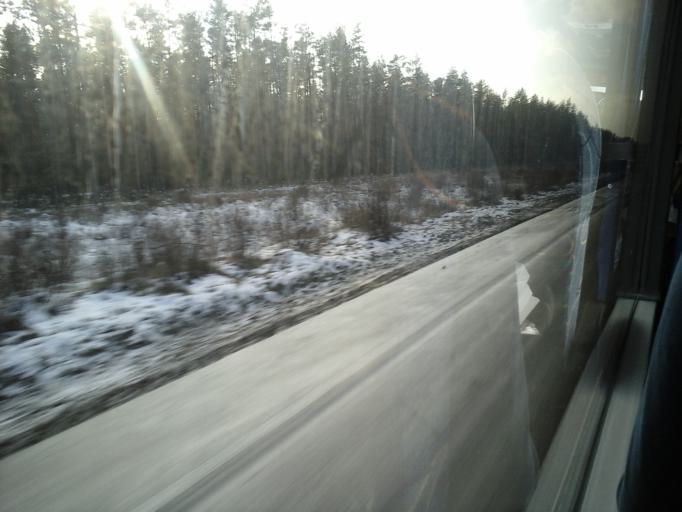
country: PL
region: Warmian-Masurian Voivodeship
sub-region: Powiat olsztynski
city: Olsztynek
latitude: 53.5868
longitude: 20.2051
